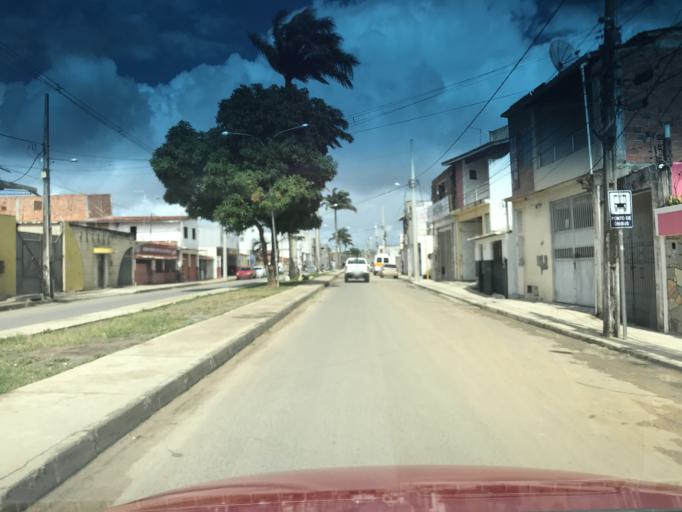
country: BR
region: Bahia
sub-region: Santo Antonio De Jesus
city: Santo Antonio de Jesus
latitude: -12.9759
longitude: -39.2746
